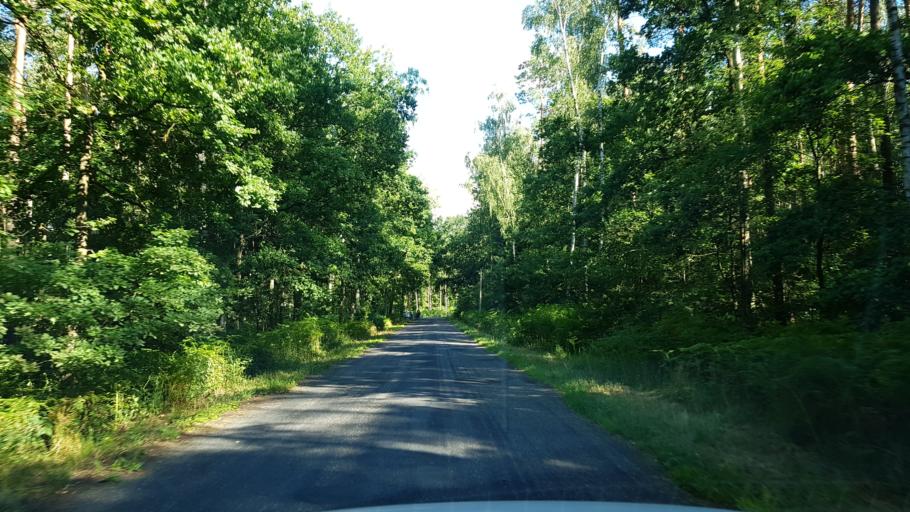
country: PL
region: West Pomeranian Voivodeship
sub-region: Powiat goleniowski
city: Goleniow
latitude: 53.5520
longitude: 14.7738
